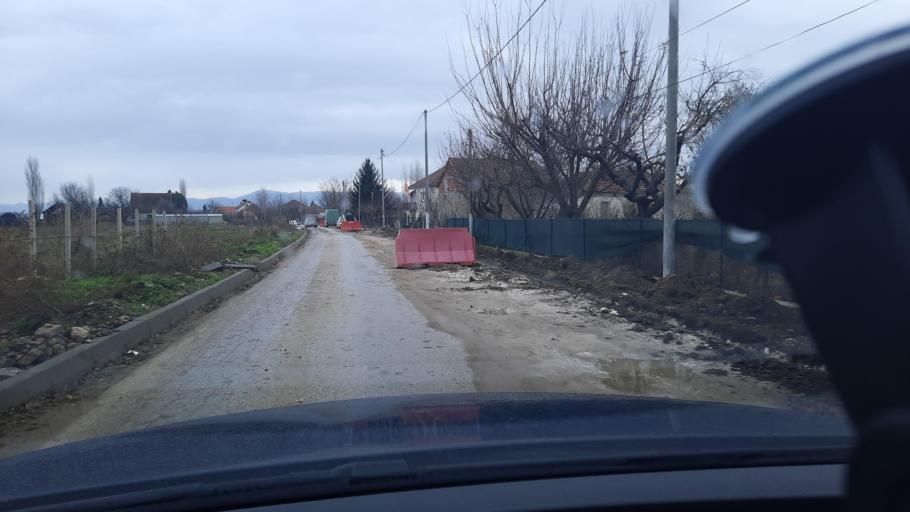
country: MK
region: Mogila
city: Mogila
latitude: 41.1101
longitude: 21.3831
